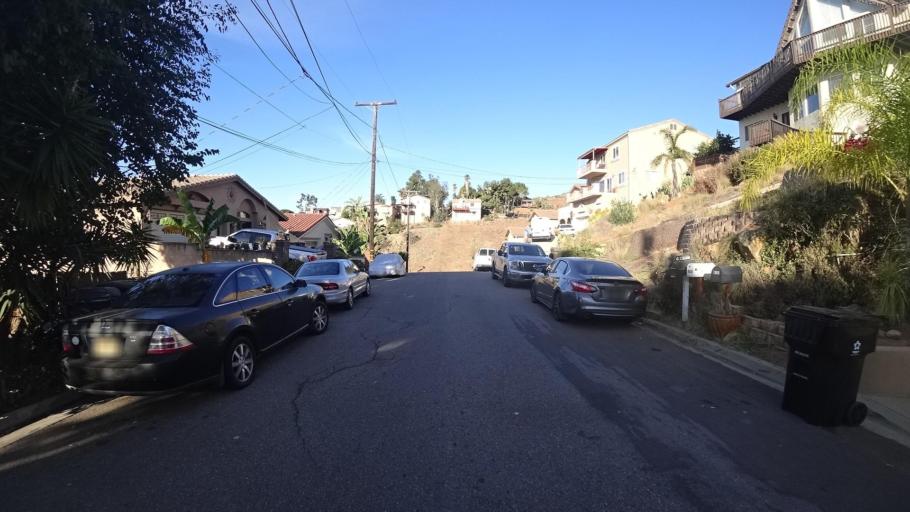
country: US
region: California
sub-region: San Diego County
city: La Presa
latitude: 32.7220
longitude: -116.9903
